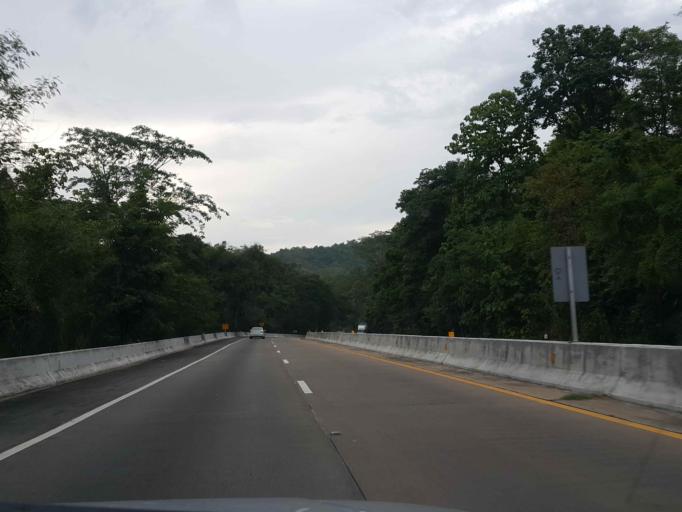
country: TH
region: Lampang
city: Hang Chat
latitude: 18.3725
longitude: 99.2352
